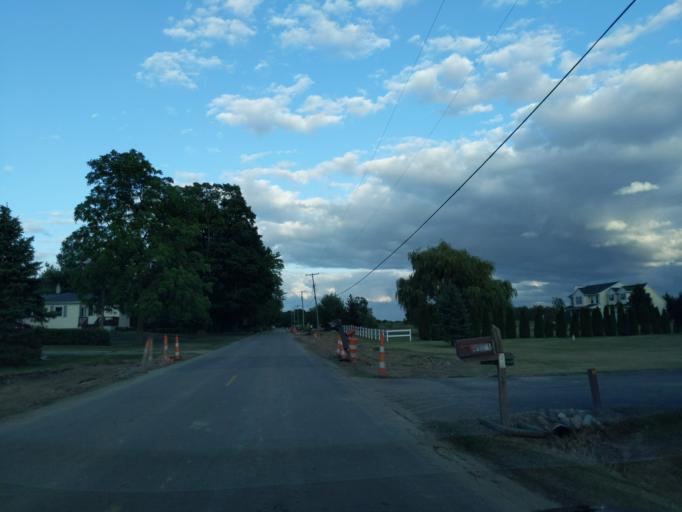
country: US
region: Michigan
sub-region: Ingham County
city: Holt
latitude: 42.5967
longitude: -84.5419
